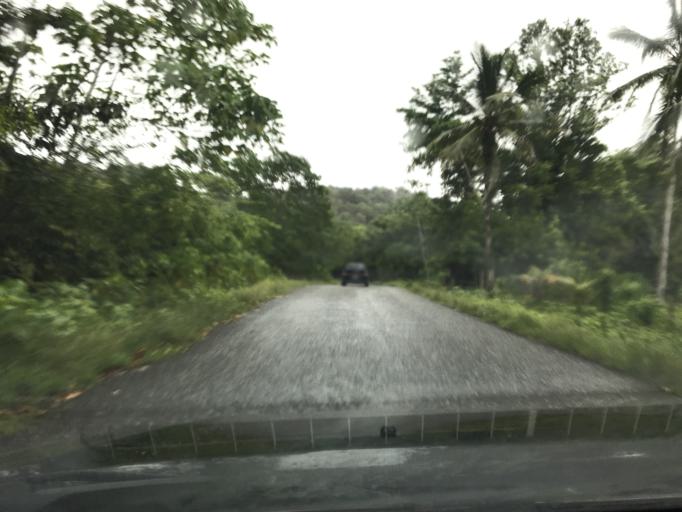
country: SB
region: Western Province
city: Gizo
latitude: -8.3128
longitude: 157.2541
